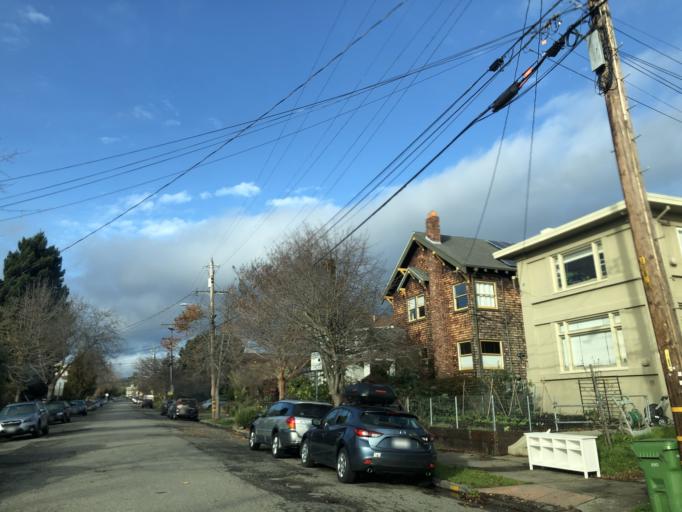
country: US
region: California
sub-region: Alameda County
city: Berkeley
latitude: 37.8515
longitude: -122.2581
